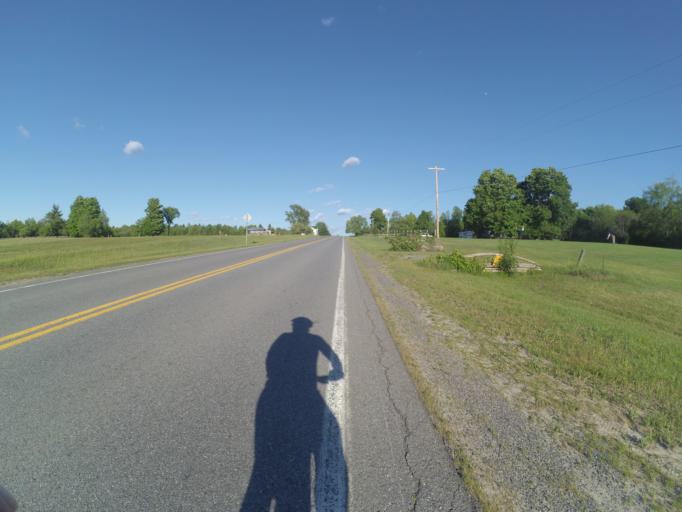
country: US
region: New York
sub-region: St. Lawrence County
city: Norwood
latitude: 44.7609
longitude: -74.8801
